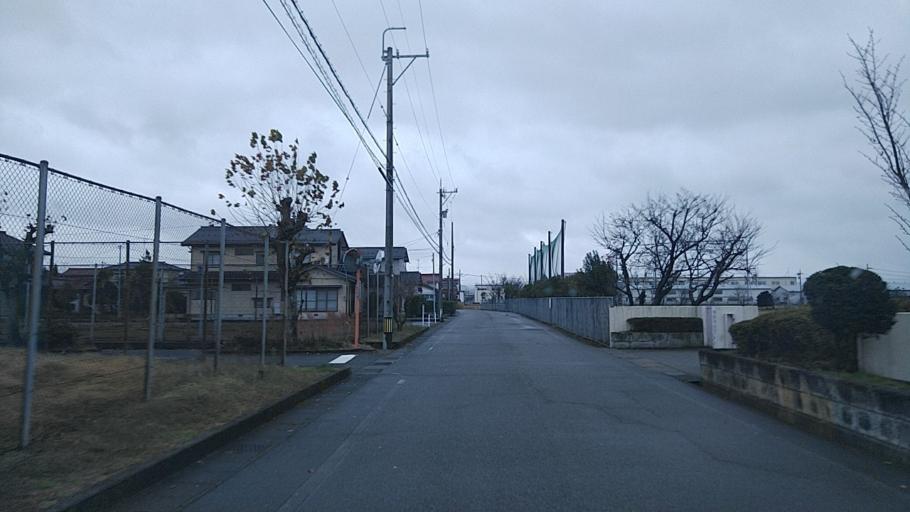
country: JP
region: Ishikawa
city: Komatsu
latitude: 36.3308
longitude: 136.3793
